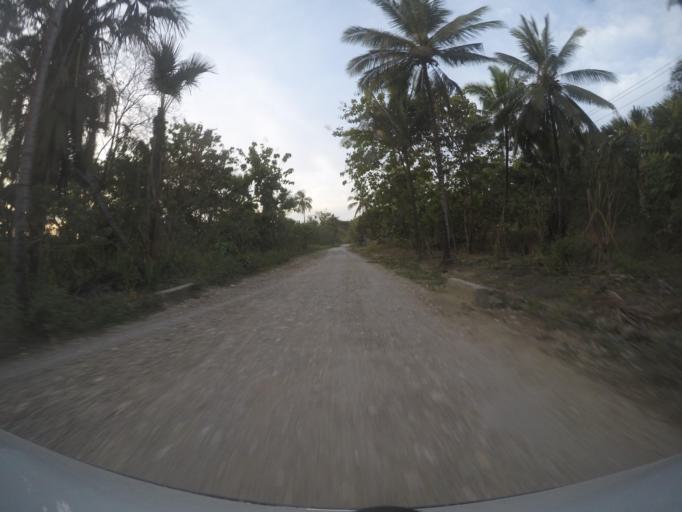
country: TL
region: Viqueque
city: Viqueque
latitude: -8.9196
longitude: 126.3973
